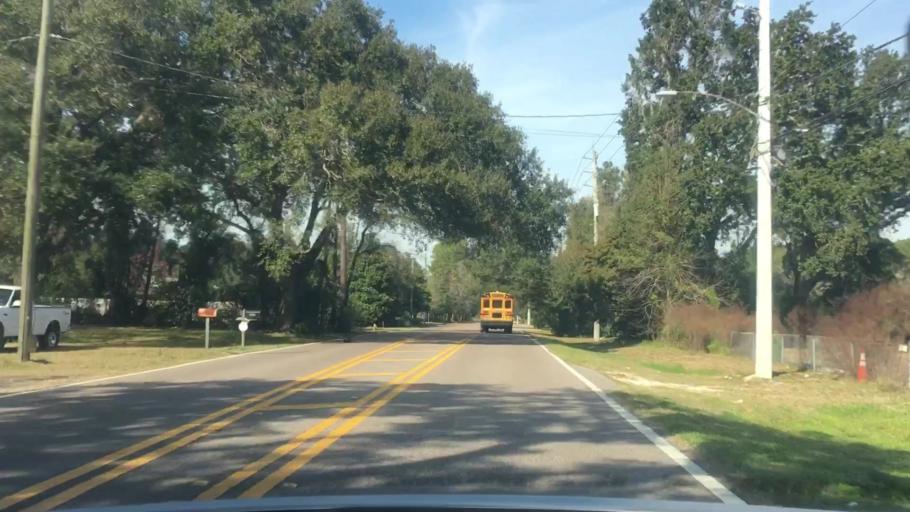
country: US
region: Florida
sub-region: Duval County
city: Jacksonville
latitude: 30.4596
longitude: -81.5599
